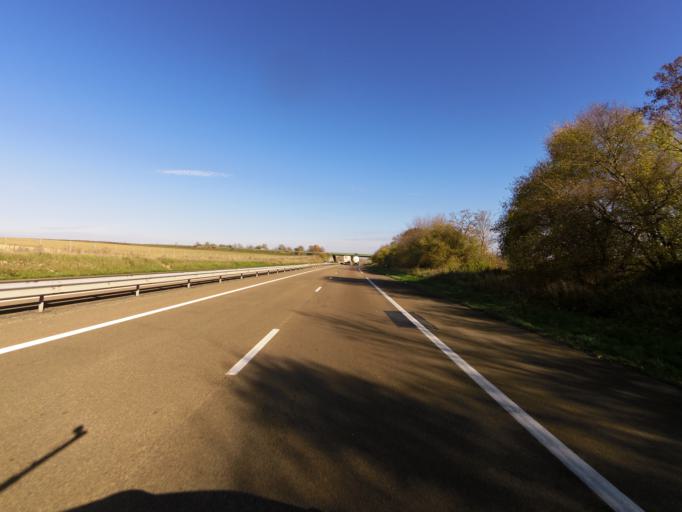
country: FR
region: Champagne-Ardenne
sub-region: Departement de la Marne
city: Fagnieres
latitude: 48.9756
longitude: 4.2855
